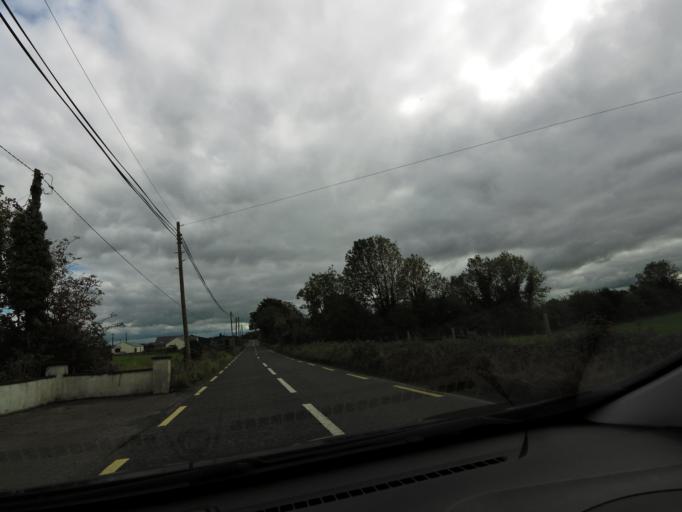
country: IE
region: Connaught
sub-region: County Galway
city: Ballinasloe
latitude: 53.3080
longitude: -8.1495
